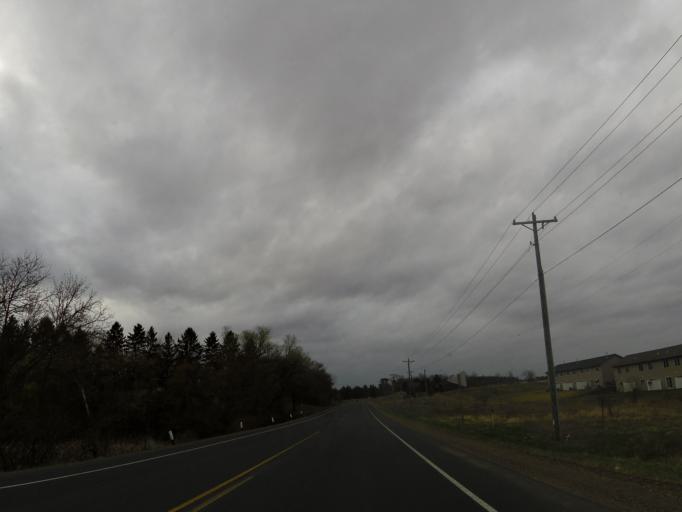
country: US
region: Wisconsin
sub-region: Saint Croix County
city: New Richmond
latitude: 45.1132
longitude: -92.5583
